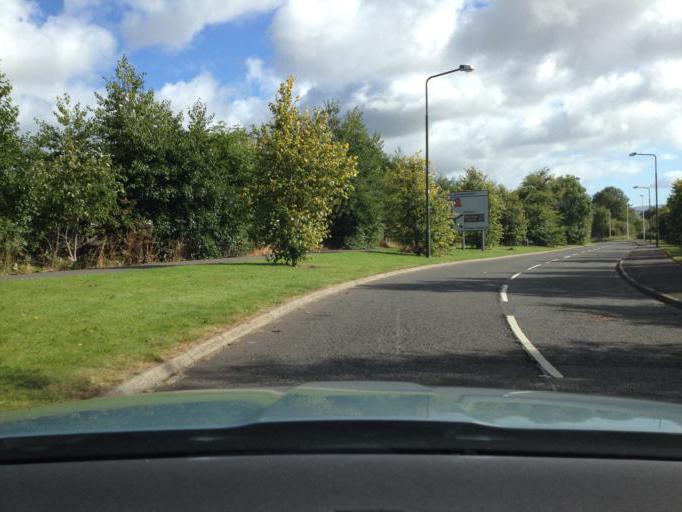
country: GB
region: Scotland
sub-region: West Lothian
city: Livingston
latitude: 55.8877
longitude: -3.5557
